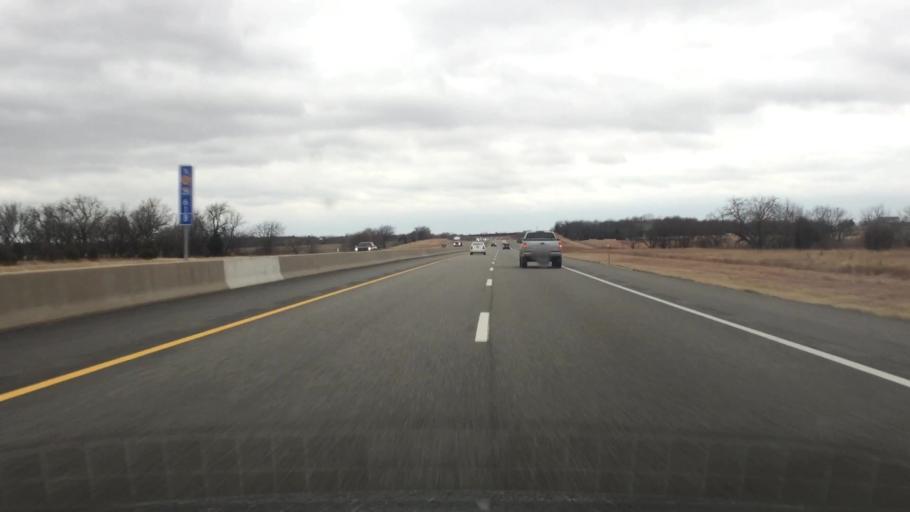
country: US
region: Kansas
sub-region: Butler County
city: Towanda
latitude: 37.7496
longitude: -97.0337
